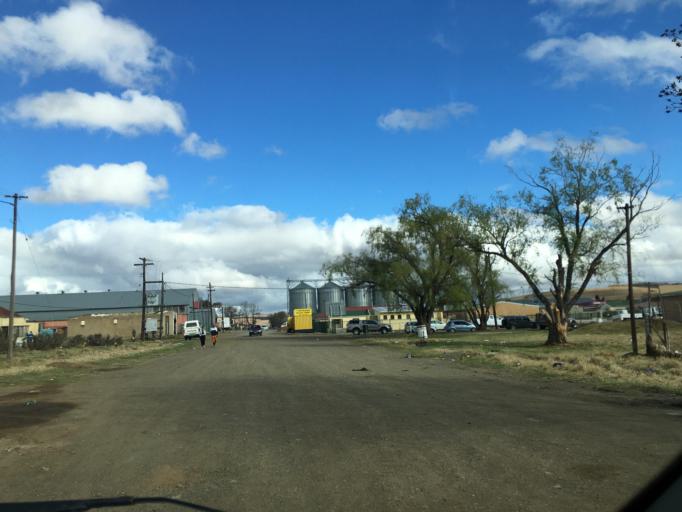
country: ZA
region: Eastern Cape
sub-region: Chris Hani District Municipality
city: Elliot
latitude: -31.3333
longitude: 27.8463
